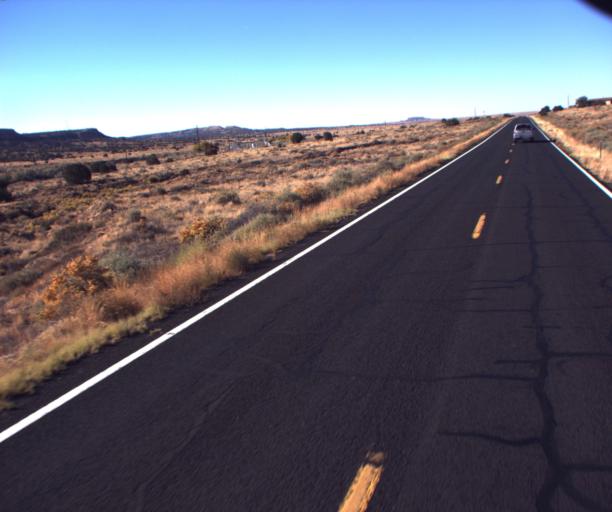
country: US
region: Arizona
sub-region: Navajo County
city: First Mesa
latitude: 35.8353
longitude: -110.2650
